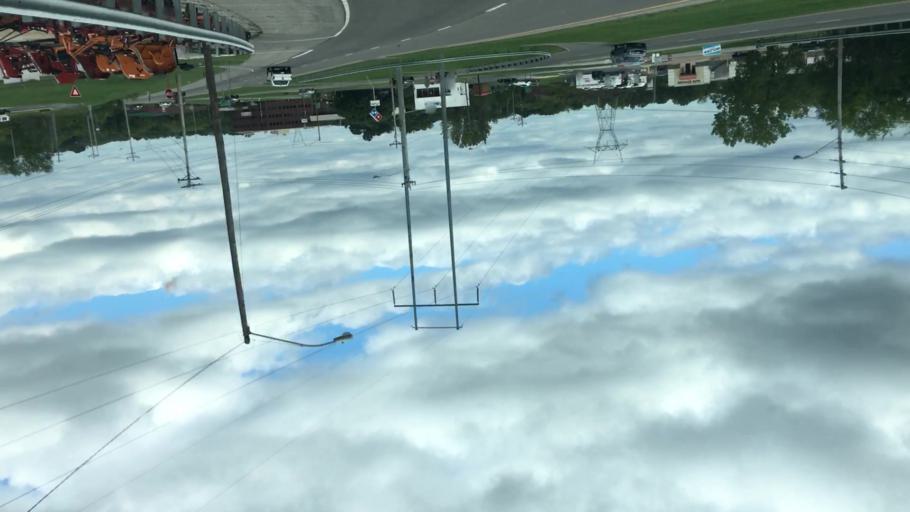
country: US
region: Tennessee
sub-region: Maury County
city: Columbia
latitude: 35.6105
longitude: -87.0692
